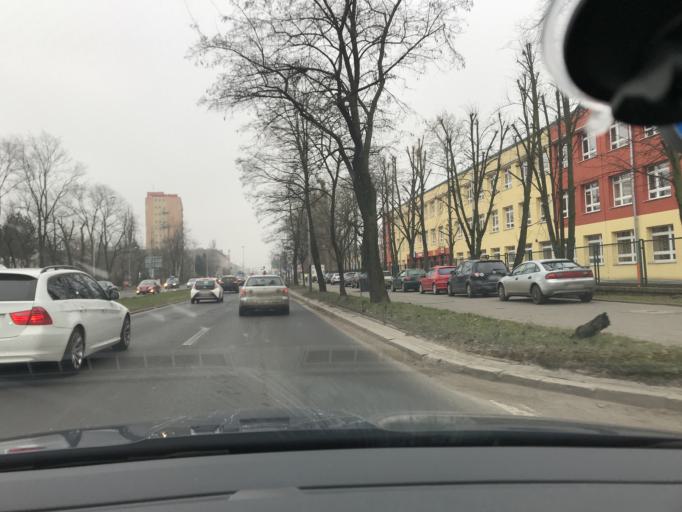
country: PL
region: Lodz Voivodeship
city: Lodz
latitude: 51.7778
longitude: 19.4816
